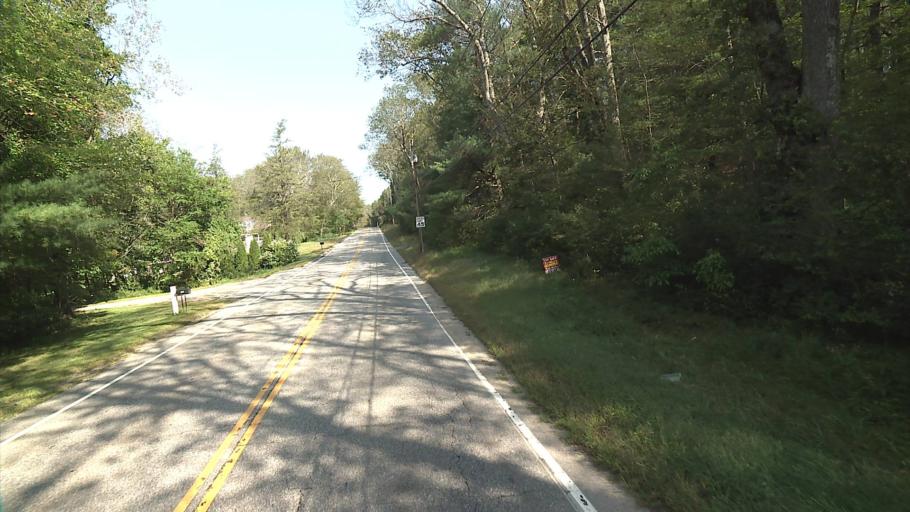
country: US
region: Connecticut
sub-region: Windham County
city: Plainfield Village
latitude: 41.6846
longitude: -71.9670
